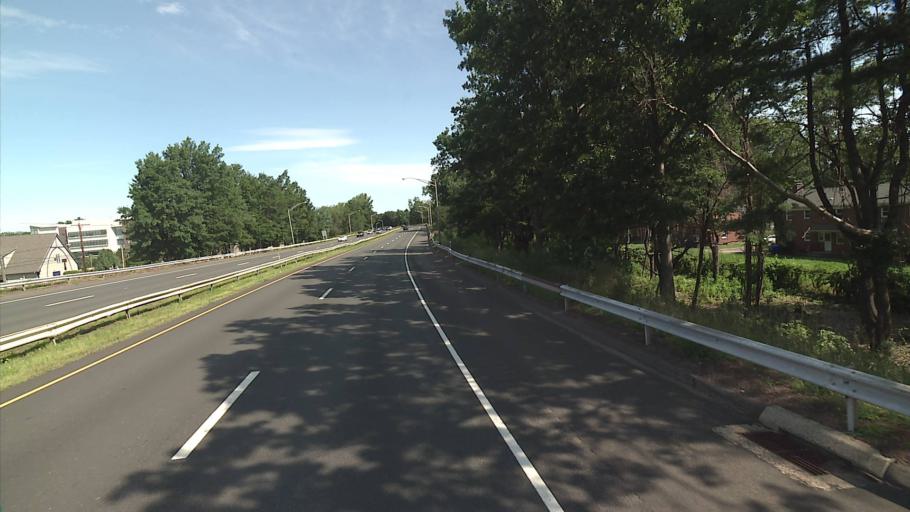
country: US
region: Connecticut
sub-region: Hartford County
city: Wethersfield
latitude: 41.7474
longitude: -72.6417
